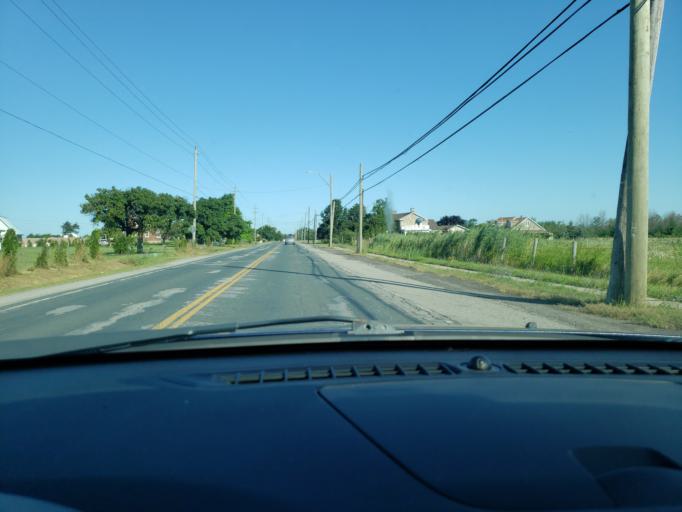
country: CA
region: Ontario
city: Hamilton
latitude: 43.2009
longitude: -79.6097
